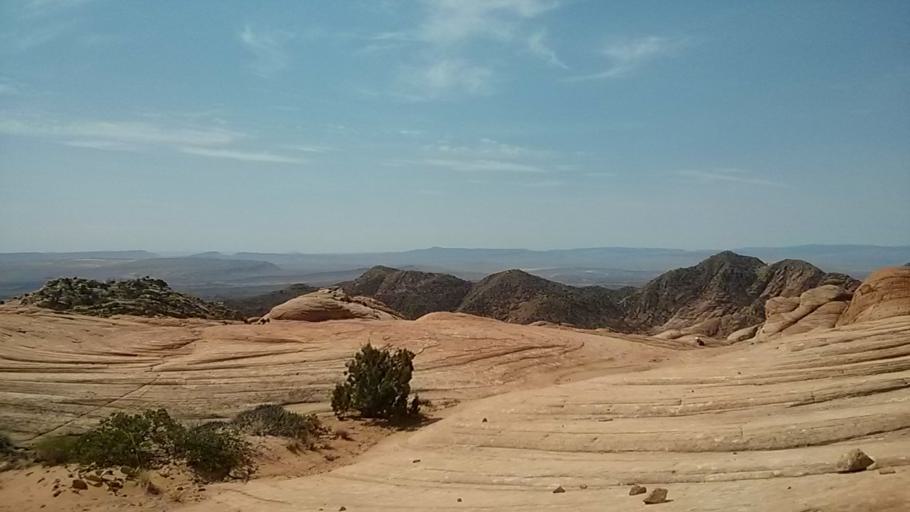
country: US
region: Utah
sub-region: Washington County
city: Washington
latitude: 37.2175
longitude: -113.4684
